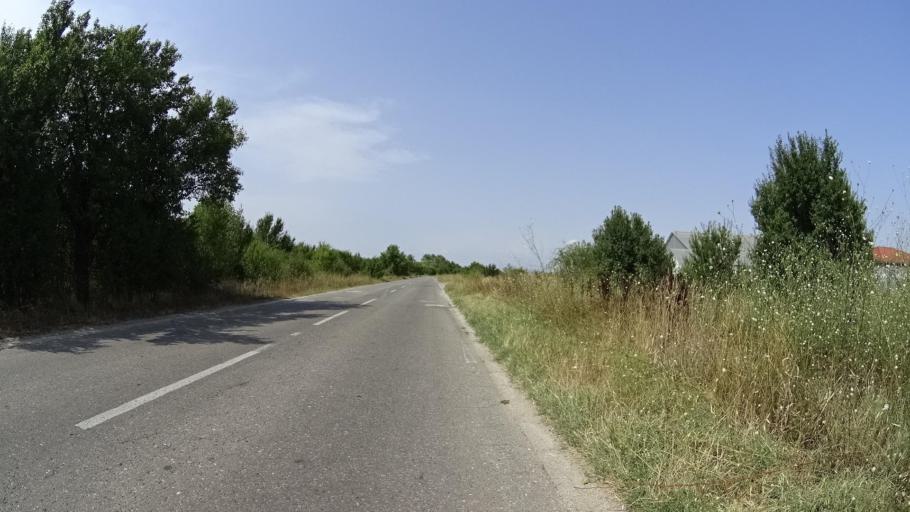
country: BG
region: Plovdiv
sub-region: Obshtina Plovdiv
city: Plovdiv
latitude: 42.2300
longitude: 24.7860
